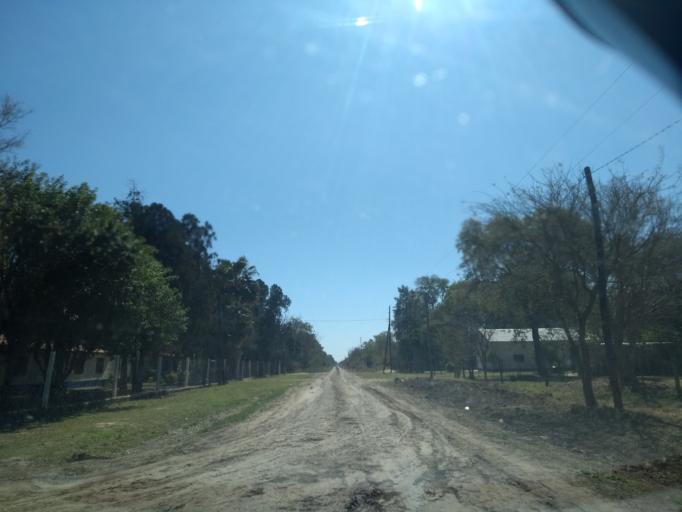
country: AR
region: Chaco
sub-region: Departamento de Quitilipi
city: Quitilipi
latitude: -26.7562
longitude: -60.2429
